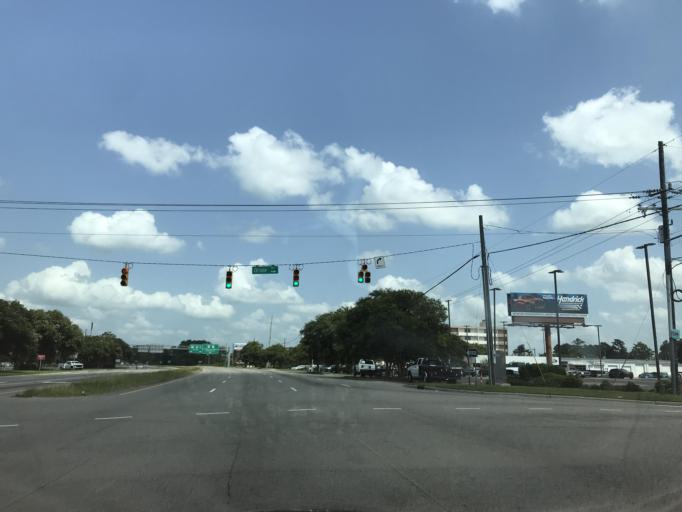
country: US
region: North Carolina
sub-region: New Hanover County
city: Kings Grant
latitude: 34.2382
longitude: -77.8716
